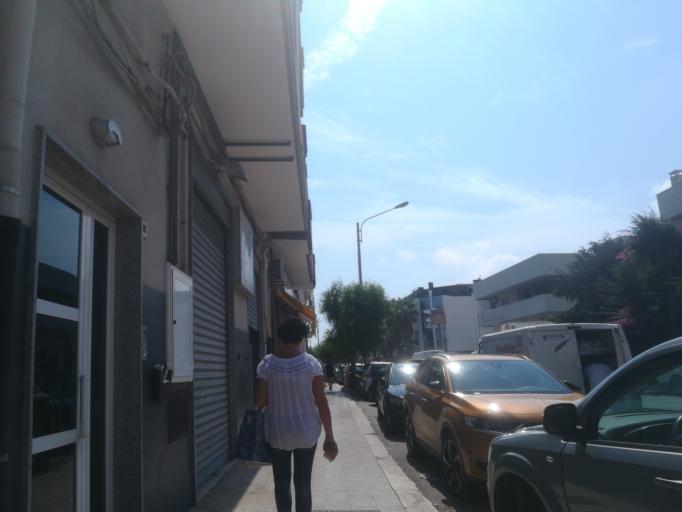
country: IT
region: Apulia
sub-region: Provincia di Bari
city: Polignano a Mare
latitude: 40.9904
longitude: 17.2212
